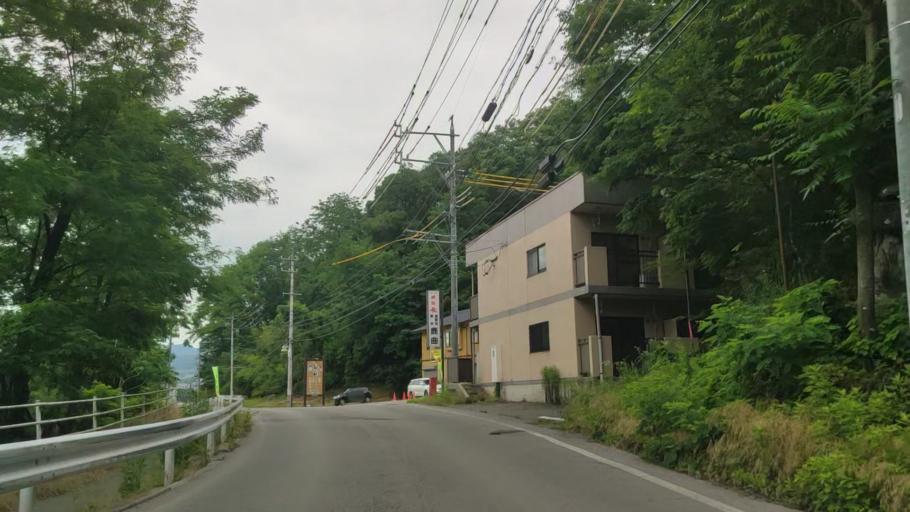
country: JP
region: Nagano
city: Kamimaruko
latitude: 36.3339
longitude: 138.3516
